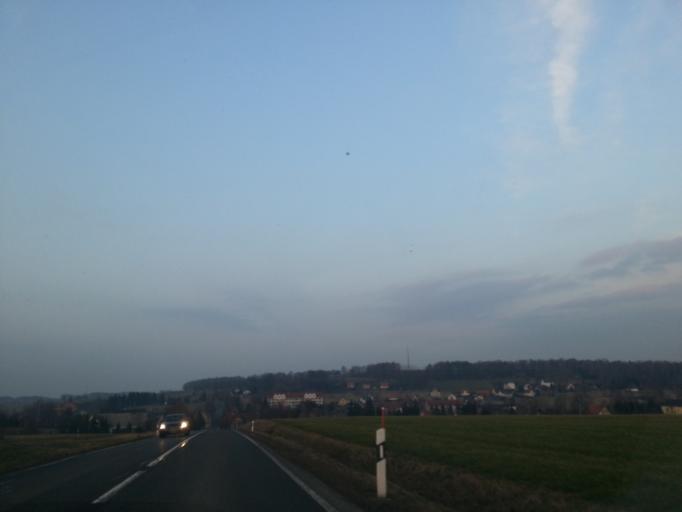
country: DE
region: Saxony
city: Niederschona
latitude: 50.9584
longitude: 13.4209
